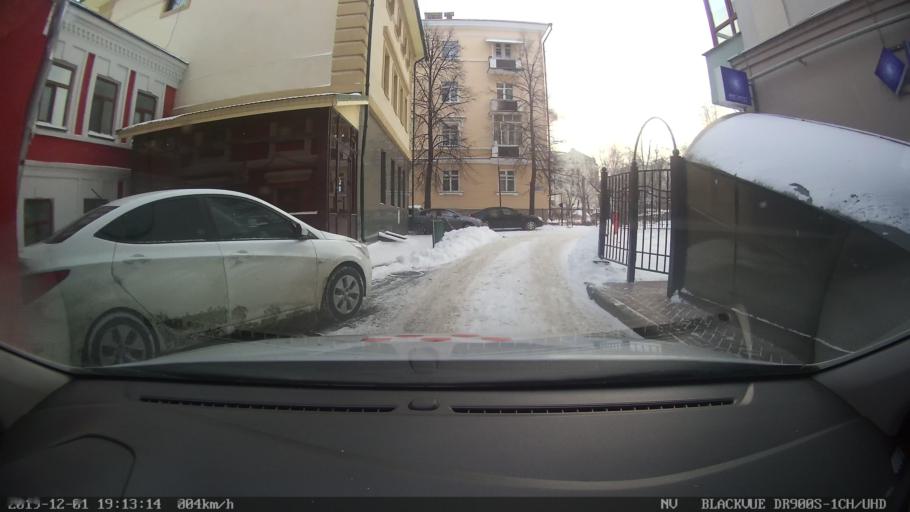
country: RU
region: Tatarstan
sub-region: Gorod Kazan'
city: Kazan
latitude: 55.7991
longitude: 49.1311
